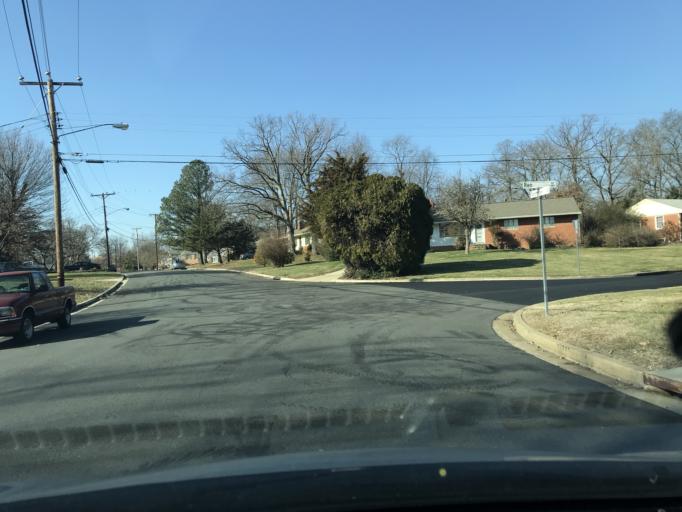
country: US
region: Virginia
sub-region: City of Fairfax
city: Fairfax
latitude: 38.8557
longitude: -77.3246
